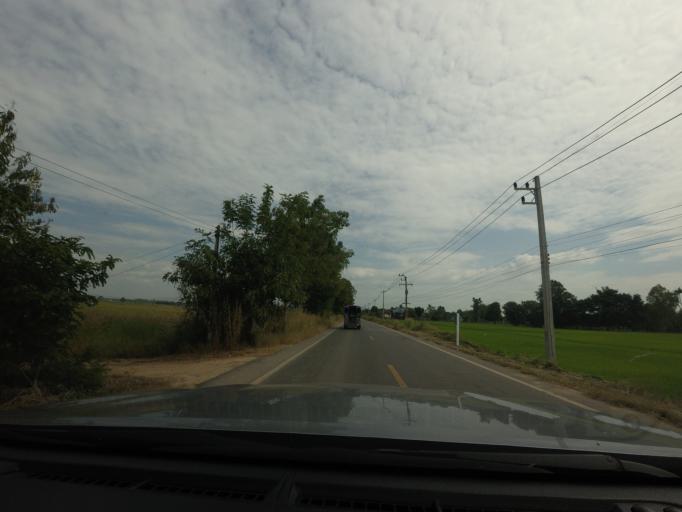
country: TH
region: Phitsanulok
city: Wang Thong
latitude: 16.7238
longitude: 100.3602
